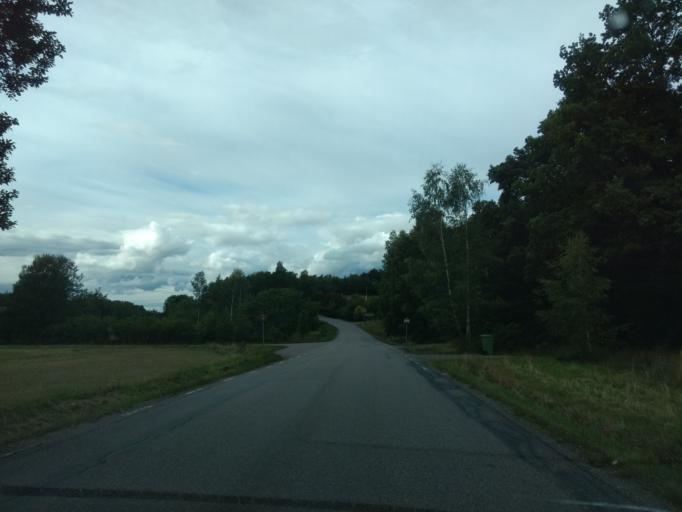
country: SE
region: Uppsala
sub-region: Habo Kommun
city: Balsta
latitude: 59.6773
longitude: 17.5369
